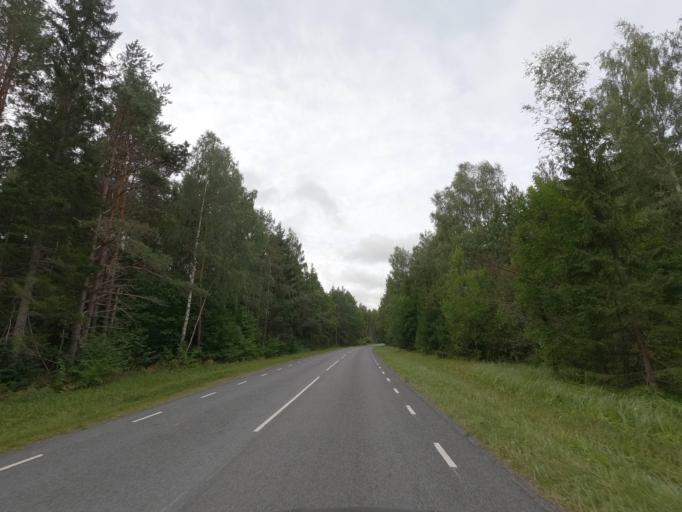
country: EE
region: Raplamaa
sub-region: Maerjamaa vald
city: Marjamaa
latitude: 59.0077
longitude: 24.5881
